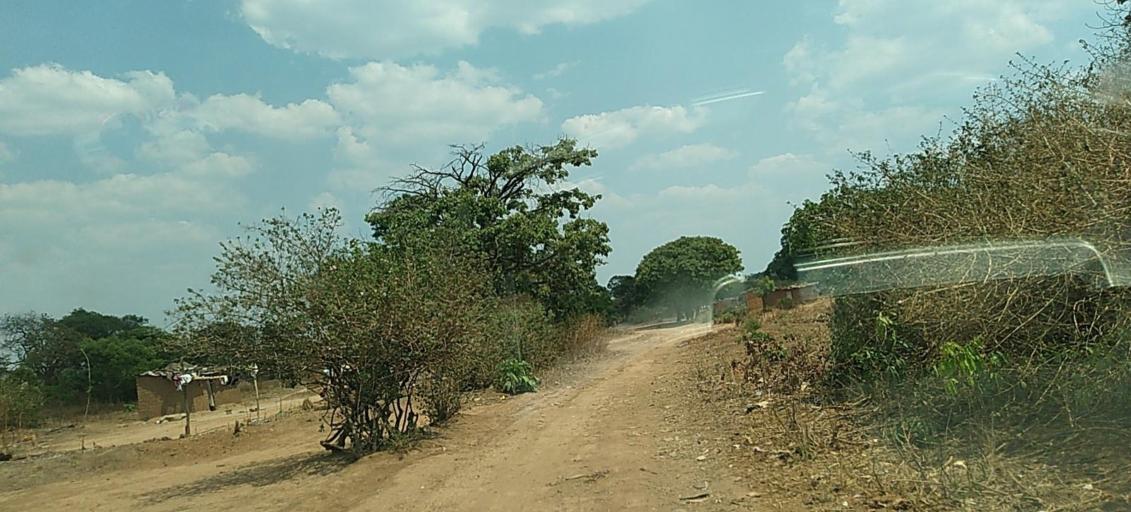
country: CD
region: Katanga
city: Kipushi
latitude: -12.0266
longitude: 27.4354
